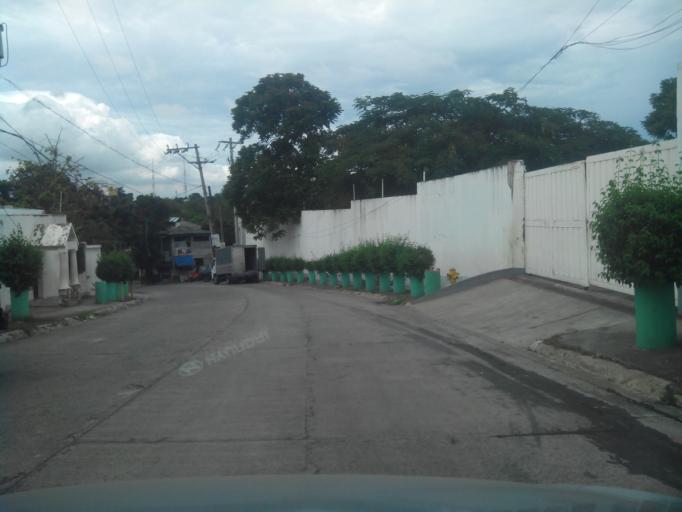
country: PH
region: Calabarzon
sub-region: Province of Rizal
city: Antipolo
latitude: 14.6034
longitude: 121.1775
